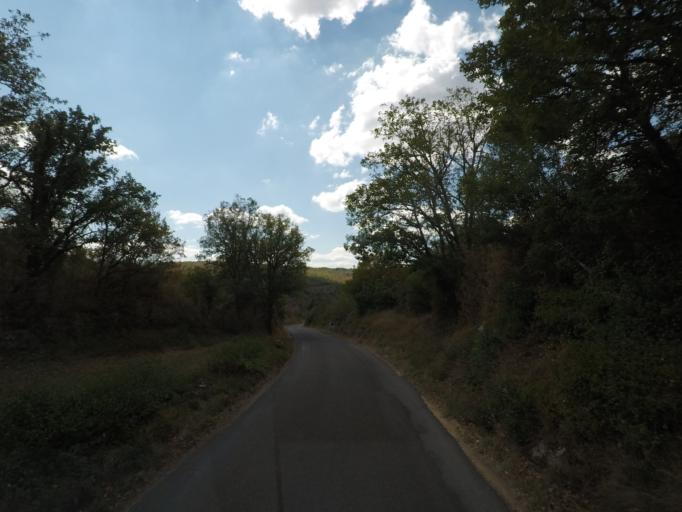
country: FR
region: Midi-Pyrenees
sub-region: Departement du Lot
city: Cajarc
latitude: 44.5160
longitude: 1.6527
